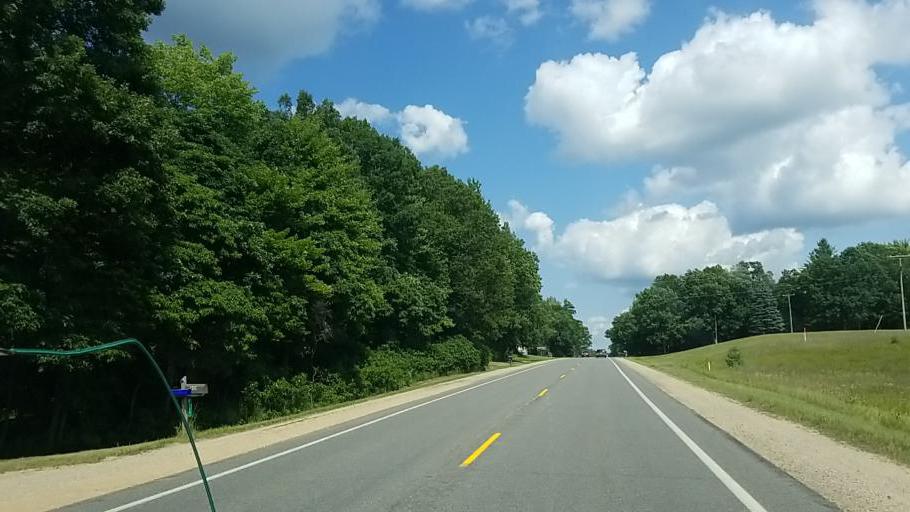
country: US
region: Michigan
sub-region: Montcalm County
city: Howard City
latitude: 43.3958
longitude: -85.5996
